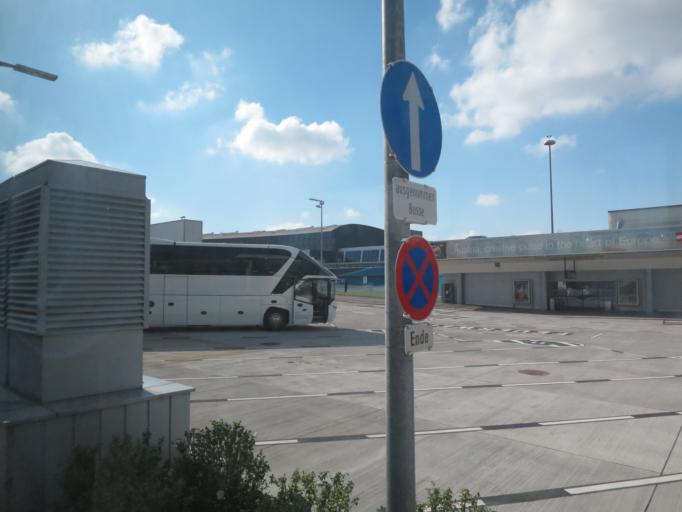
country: AT
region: Lower Austria
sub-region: Politischer Bezirk Wien-Umgebung
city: Fischamend Dorf
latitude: 48.1217
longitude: 16.5623
